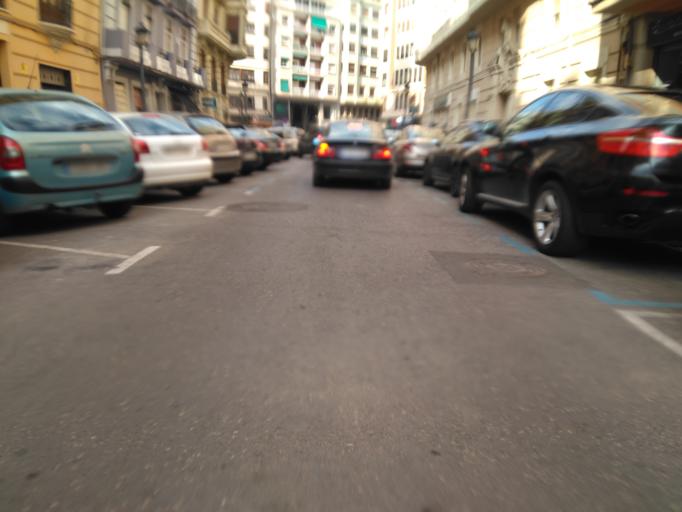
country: ES
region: Valencia
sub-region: Provincia de Valencia
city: Valencia
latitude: 39.4649
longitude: -0.3768
